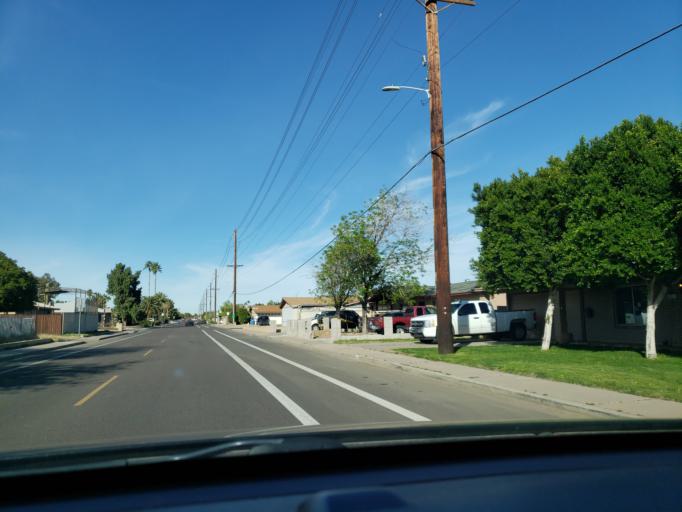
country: US
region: Arizona
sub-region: Maricopa County
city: Glendale
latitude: 33.5692
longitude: -112.1429
